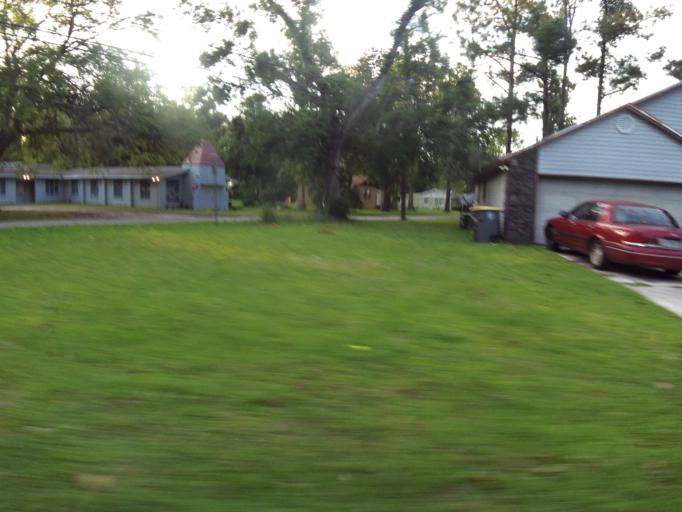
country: US
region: Florida
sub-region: Duval County
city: Jacksonville
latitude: 30.2983
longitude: -81.6261
